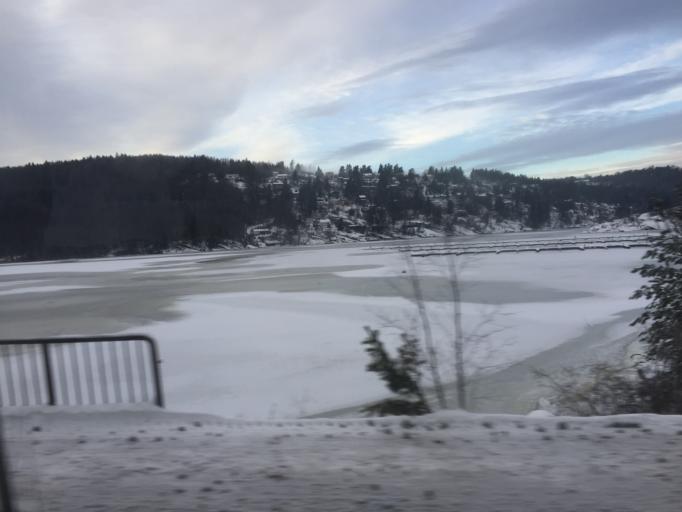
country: NO
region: Akershus
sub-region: As
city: As
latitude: 59.7287
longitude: 10.7333
